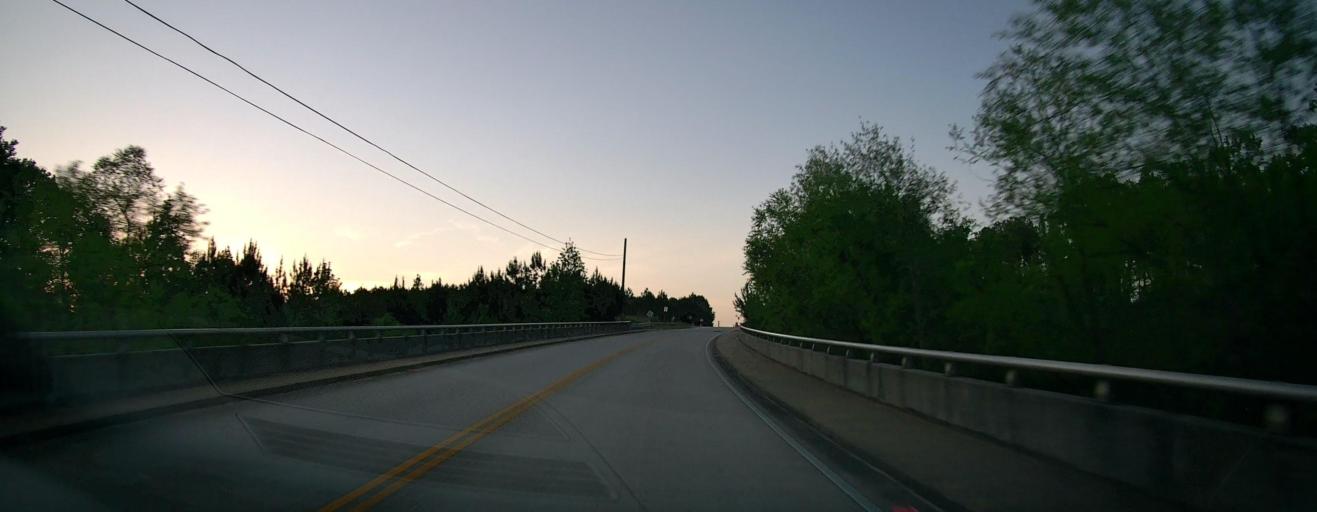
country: US
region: Georgia
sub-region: Henry County
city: Stockbridge
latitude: 33.5028
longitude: -84.2251
